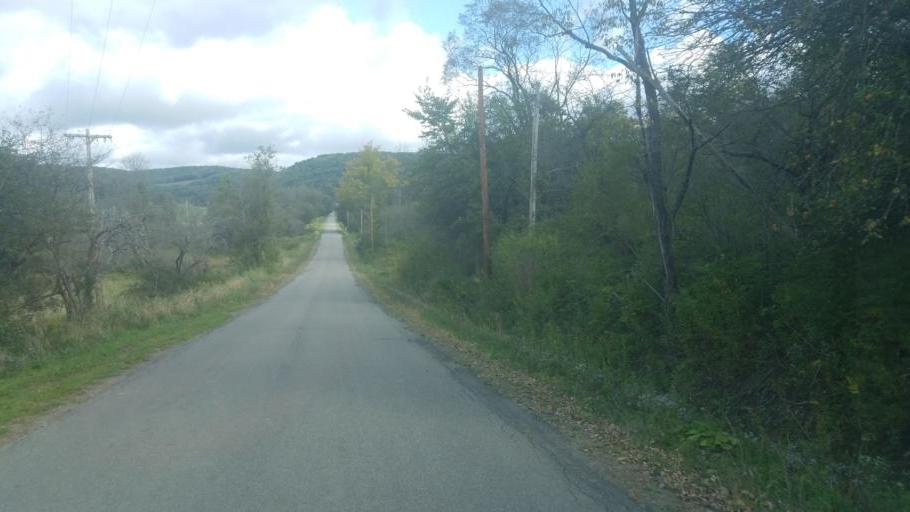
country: US
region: New York
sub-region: Cattaraugus County
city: Weston Mills
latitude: 42.1253
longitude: -78.3441
